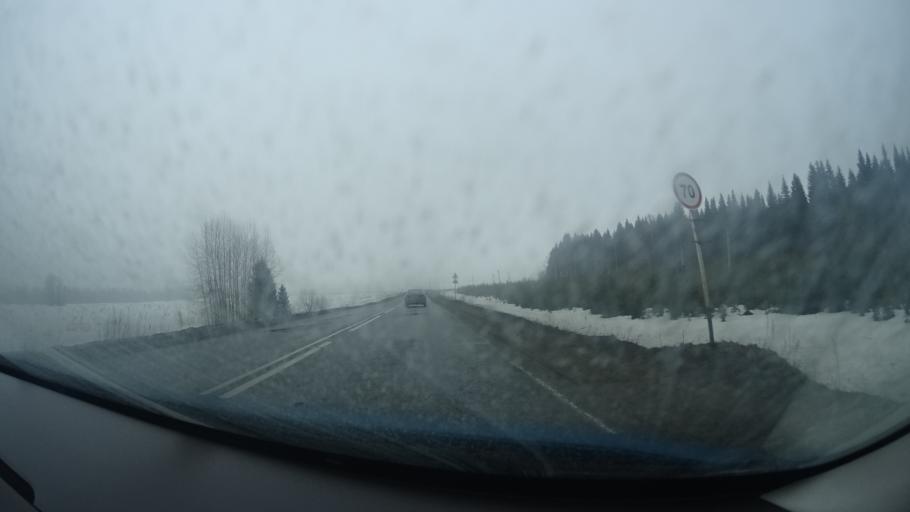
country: RU
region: Perm
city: Kuyeda
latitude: 56.4700
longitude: 55.7019
